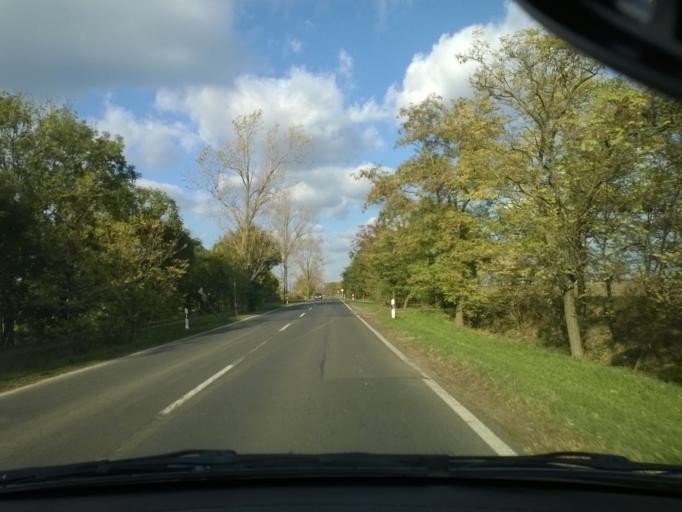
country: HU
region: Csongrad
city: Hodmezovasarhely
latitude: 46.4678
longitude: 20.3127
